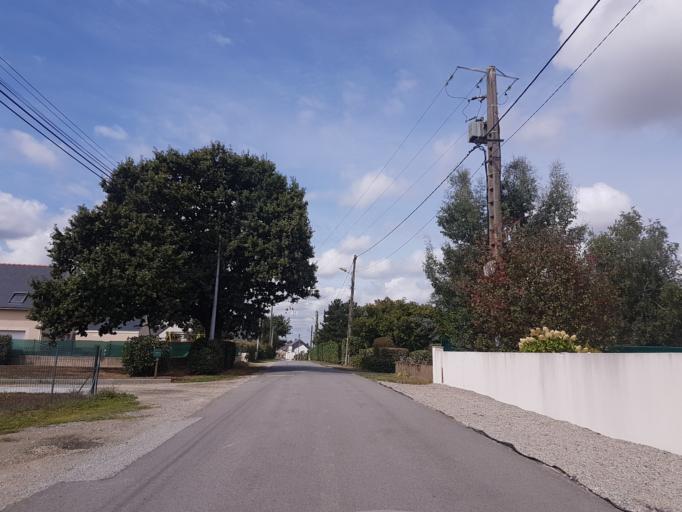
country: FR
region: Pays de la Loire
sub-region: Departement de la Loire-Atlantique
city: Petit-Mars
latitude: 47.3873
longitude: -1.4309
